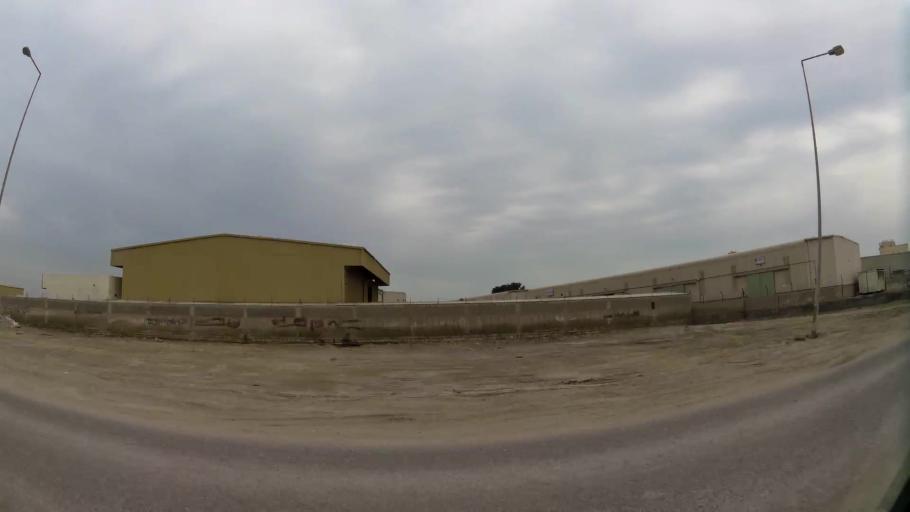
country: BH
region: Northern
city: Sitrah
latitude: 26.1755
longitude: 50.6097
